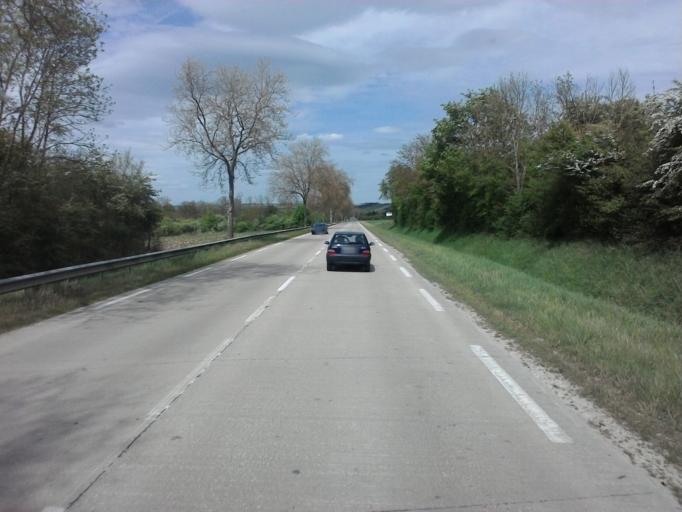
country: FR
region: Bourgogne
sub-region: Departement de l'Yonne
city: Augy
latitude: 47.7530
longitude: 3.6062
